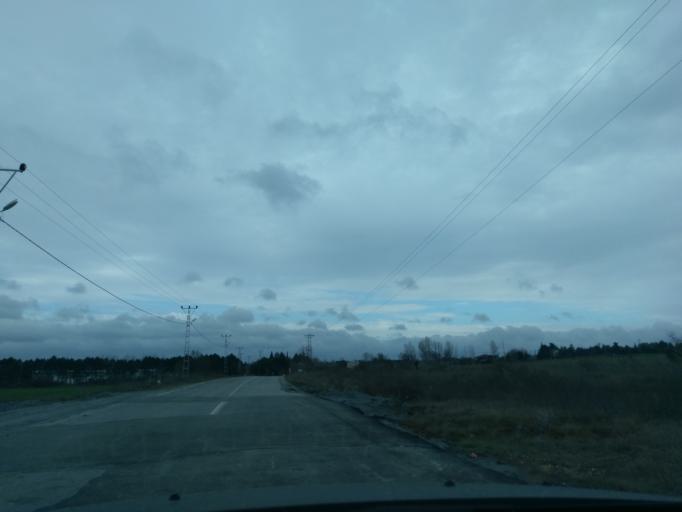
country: TR
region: Istanbul
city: Catalca
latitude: 41.2070
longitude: 28.3815
